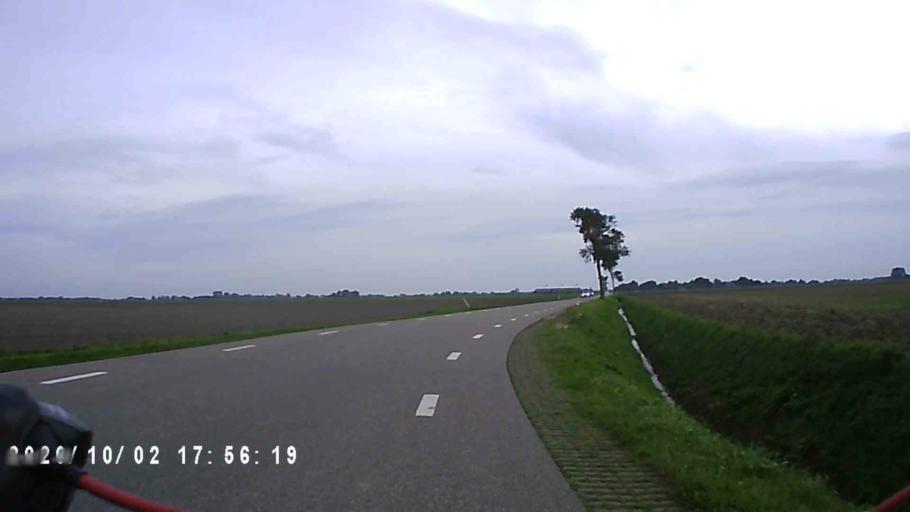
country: NL
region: Groningen
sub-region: Gemeente Zuidhorn
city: Oldehove
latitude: 53.3264
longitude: 6.4258
